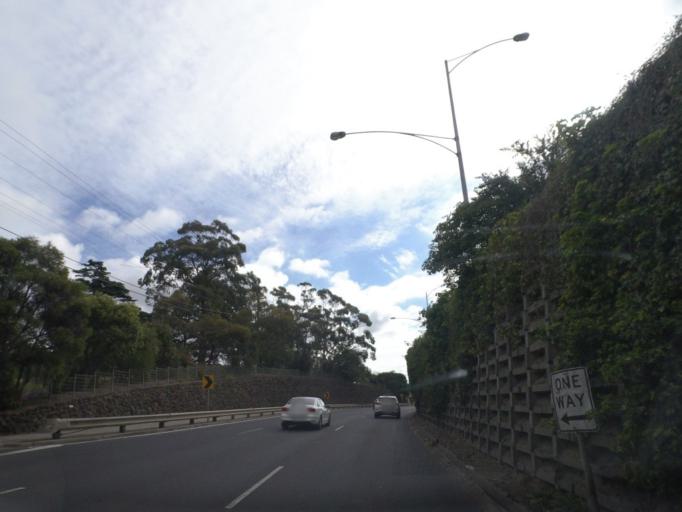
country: AU
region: Victoria
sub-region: Maroondah
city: Heathmont
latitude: -37.8320
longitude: 145.2430
